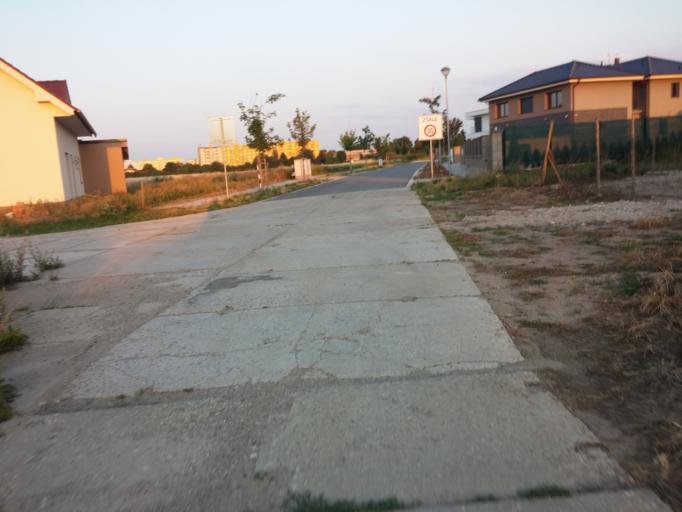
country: CZ
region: Central Bohemia
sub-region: Okres Nymburk
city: Podebrady
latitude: 50.1554
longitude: 15.1244
